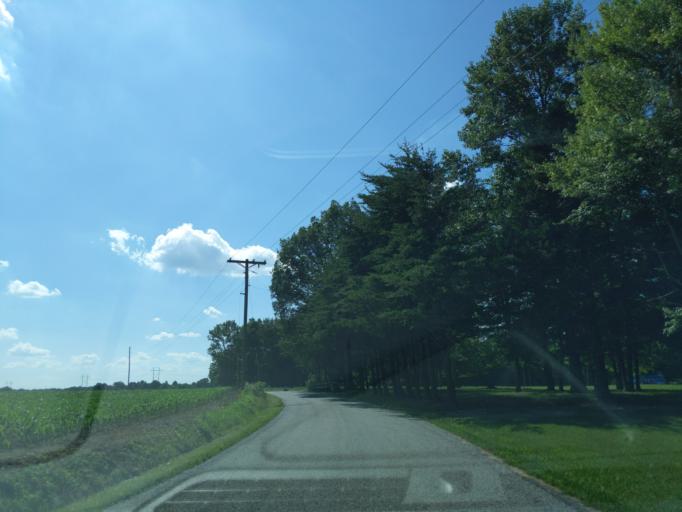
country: US
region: Indiana
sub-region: Ripley County
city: Osgood
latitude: 39.1895
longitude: -85.4147
